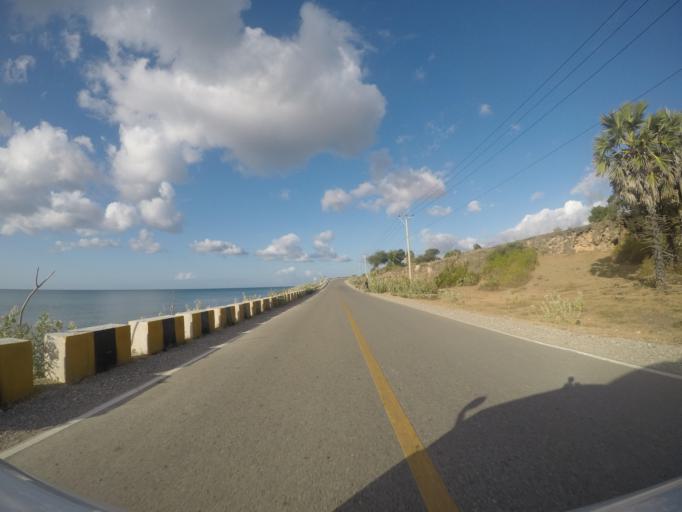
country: TL
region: Lautem
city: Lospalos
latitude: -8.3714
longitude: 126.8791
